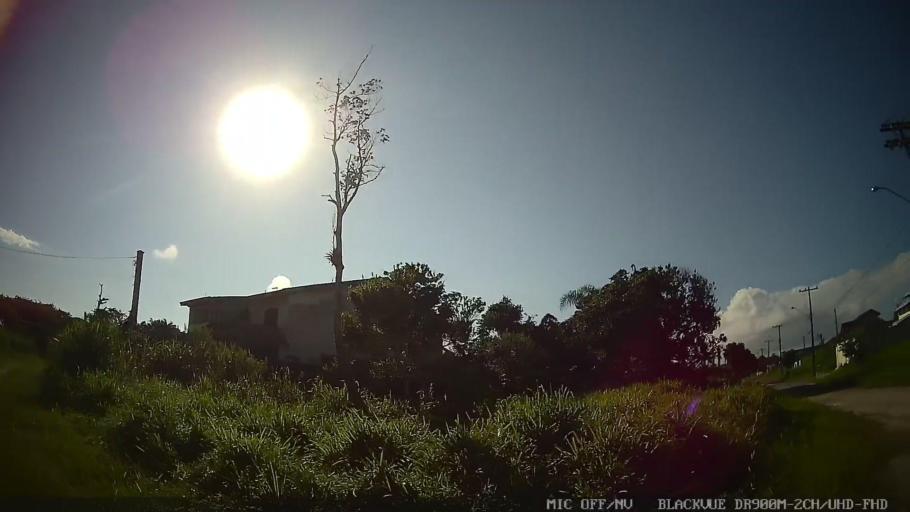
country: BR
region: Sao Paulo
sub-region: Peruibe
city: Peruibe
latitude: -24.2666
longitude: -46.9406
